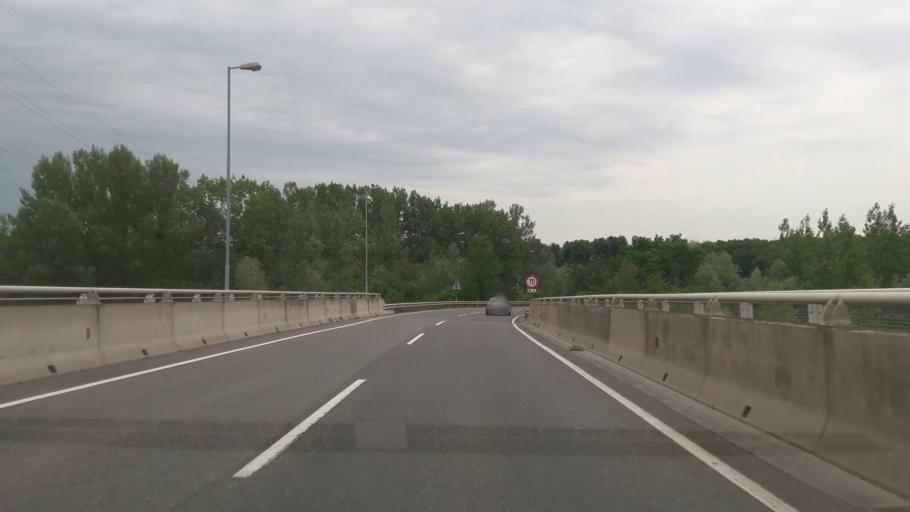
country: AT
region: Lower Austria
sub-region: Politischer Bezirk Tulln
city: Tulln
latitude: 48.3363
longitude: 16.0277
